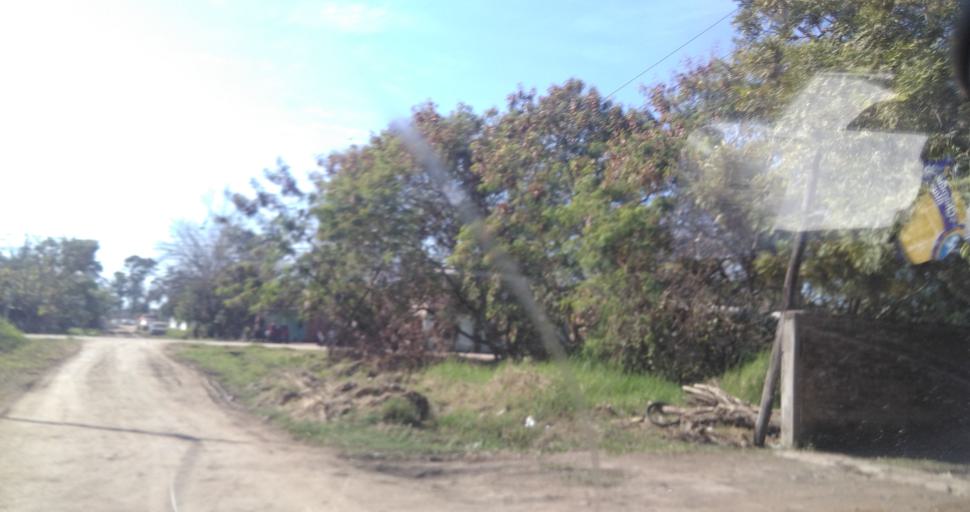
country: AR
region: Chaco
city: Fontana
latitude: -27.4447
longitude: -59.0305
